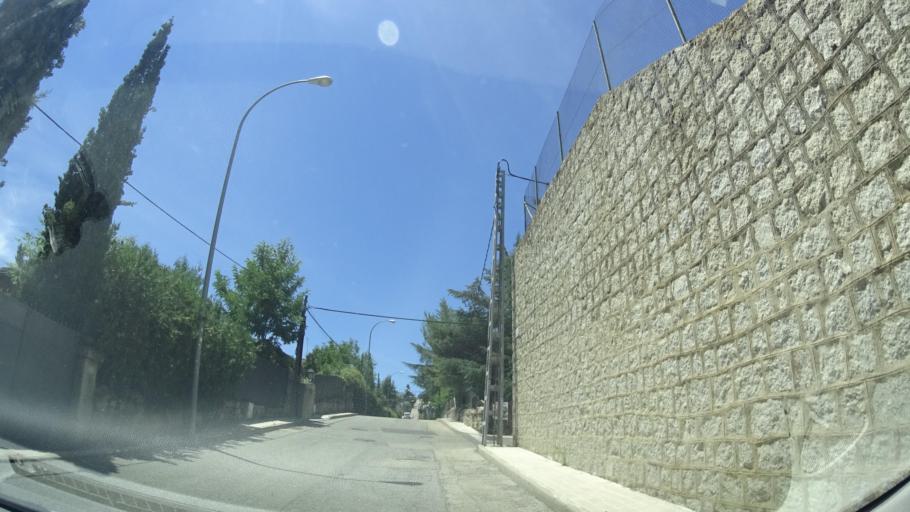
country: ES
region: Madrid
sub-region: Provincia de Madrid
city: Galapagar
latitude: 40.5963
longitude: -3.9864
